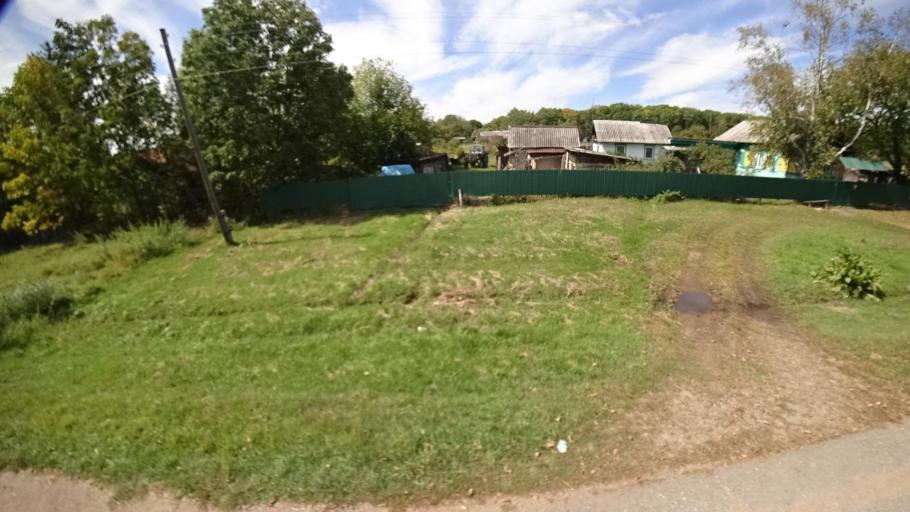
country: RU
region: Primorskiy
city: Yakovlevka
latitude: 44.6476
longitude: 133.5968
